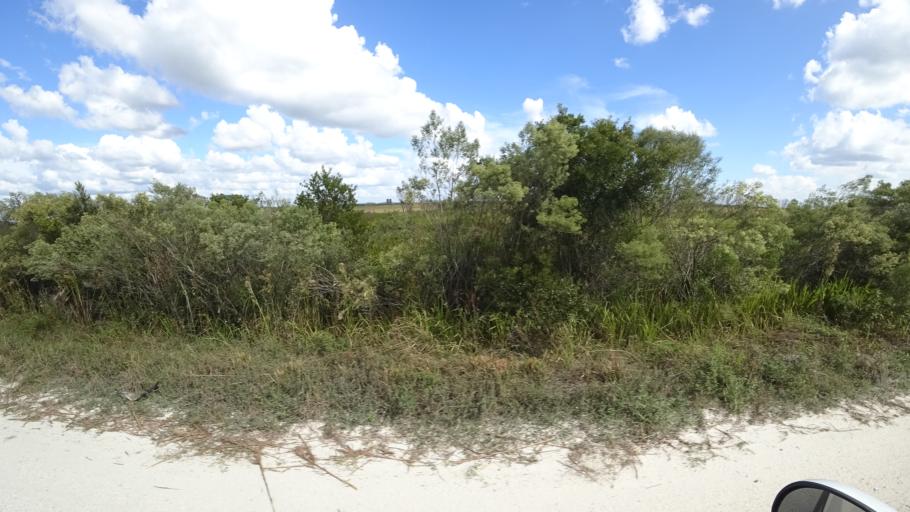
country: US
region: Florida
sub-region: DeSoto County
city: Arcadia
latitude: 27.3239
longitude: -82.1050
